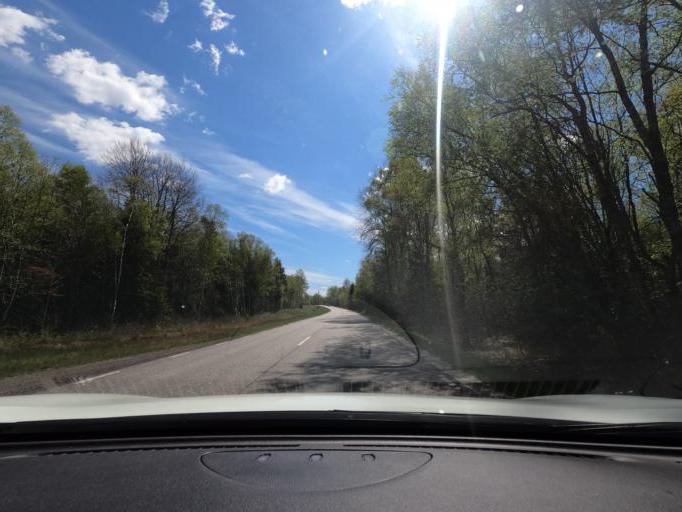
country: SE
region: Halland
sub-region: Kungsbacka Kommun
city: Fjaeras kyrkby
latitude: 57.3991
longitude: 12.2349
